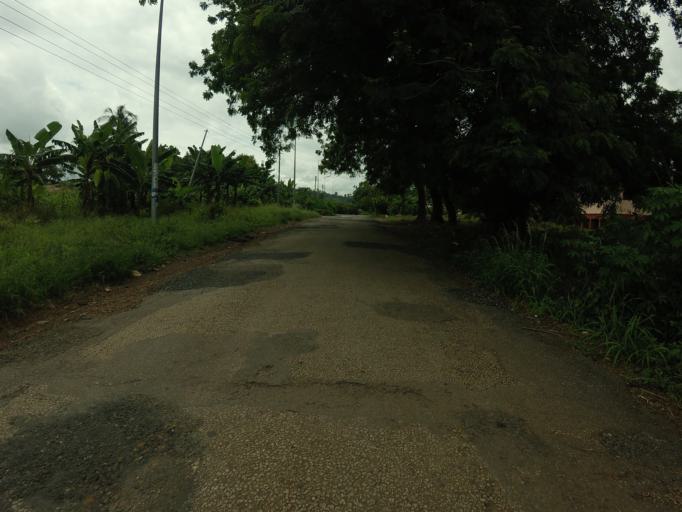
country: GH
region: Volta
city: Ho
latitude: 6.6055
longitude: 0.4617
